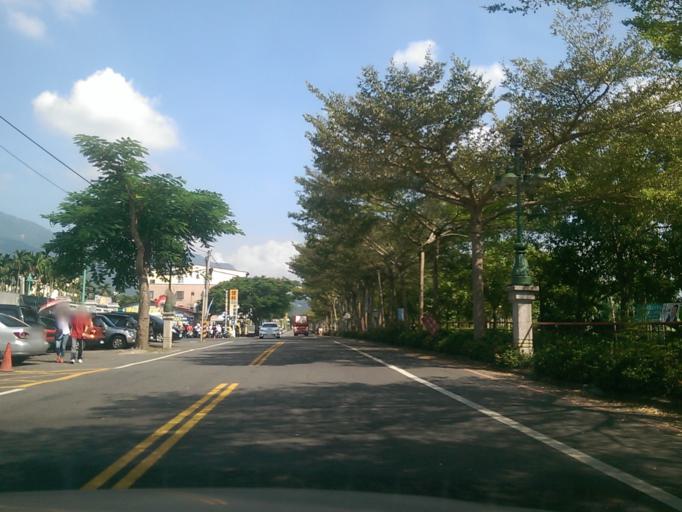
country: TW
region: Taiwan
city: Lugu
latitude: 23.8265
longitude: 120.7882
